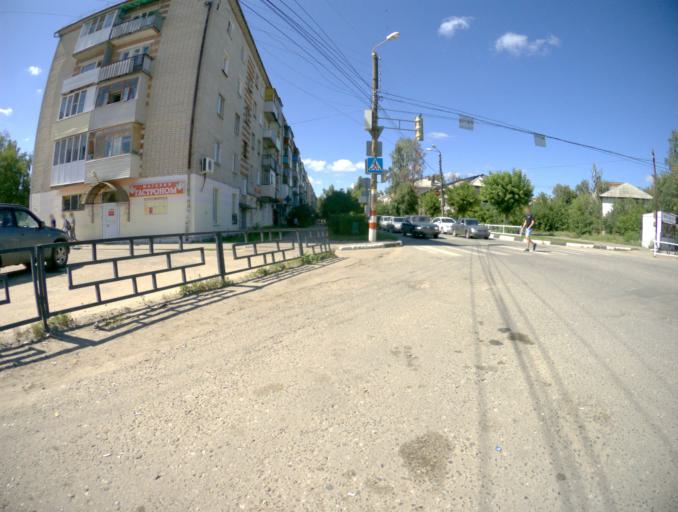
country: RU
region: Nizjnij Novgorod
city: Bor
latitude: 56.3554
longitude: 44.0728
